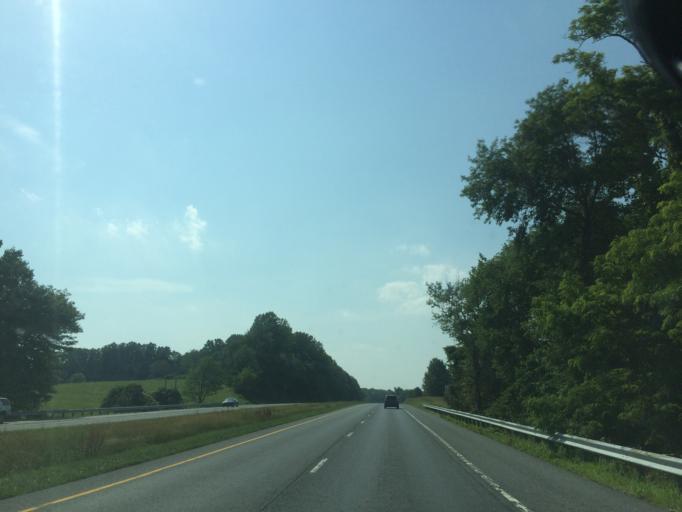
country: US
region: Maryland
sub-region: Howard County
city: Columbia
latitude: 39.2914
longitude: -76.8925
